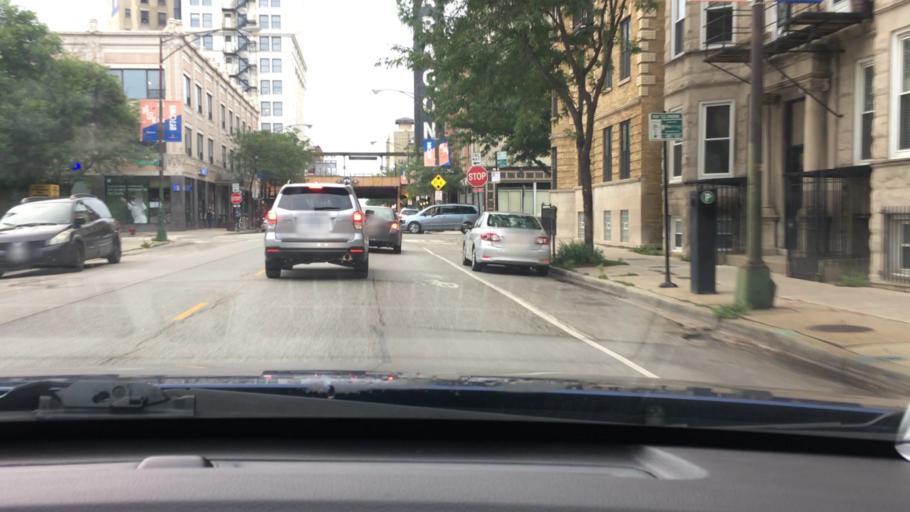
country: US
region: Illinois
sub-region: Cook County
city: Evanston
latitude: 41.9691
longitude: -87.6571
